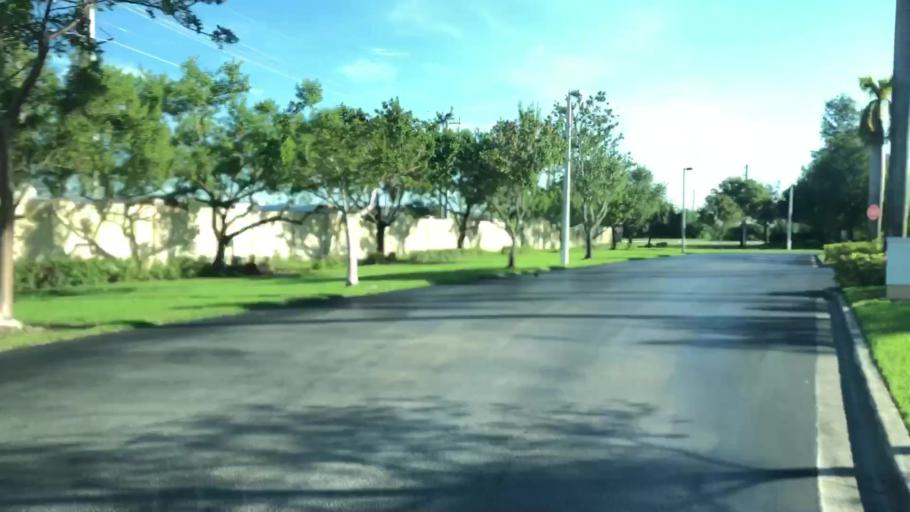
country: US
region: Florida
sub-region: Miami-Dade County
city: Country Club
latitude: 25.9774
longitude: -80.3022
